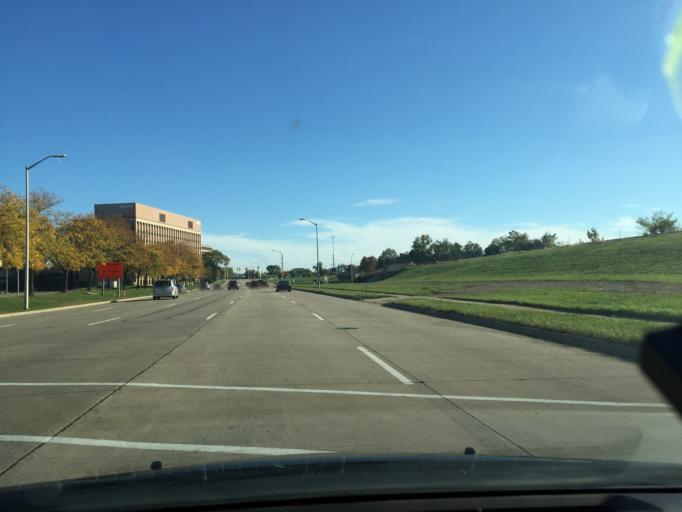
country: US
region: Michigan
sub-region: Oakland County
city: Pontiac
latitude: 42.6361
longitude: -83.2944
